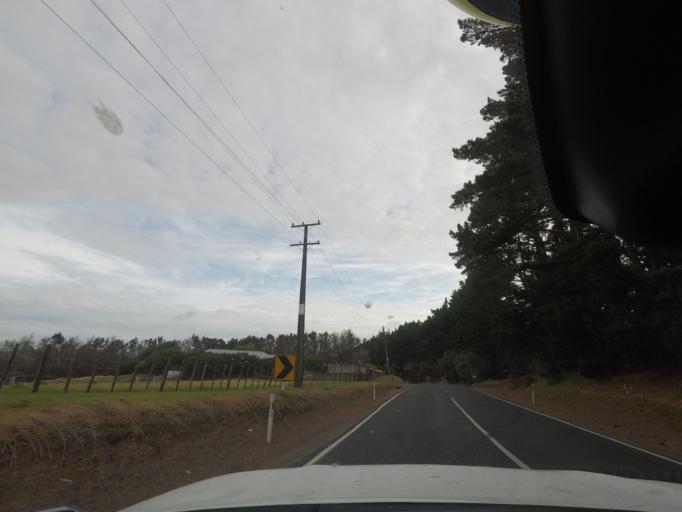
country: NZ
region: Auckland
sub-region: Auckland
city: Parakai
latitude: -36.5366
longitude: 174.2919
